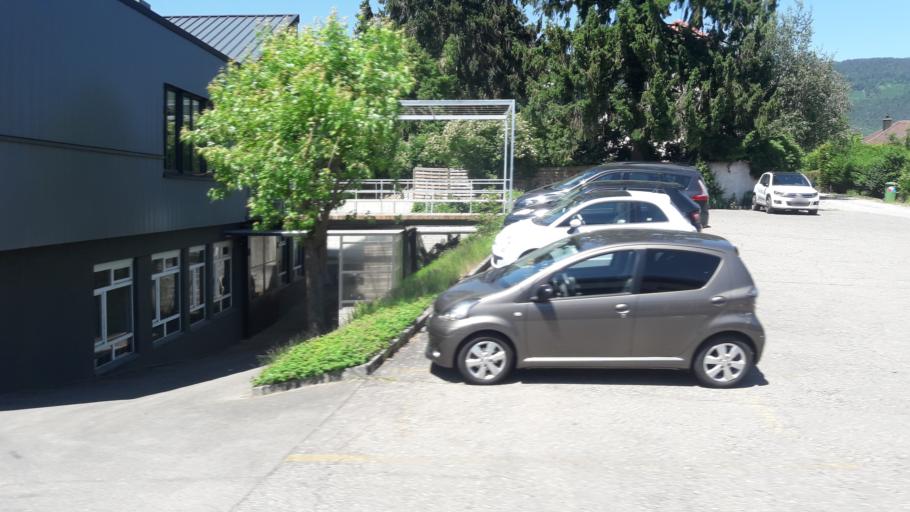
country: CH
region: Bern
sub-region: Biel/Bienne District
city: Bellmund
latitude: 47.0985
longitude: 7.2157
